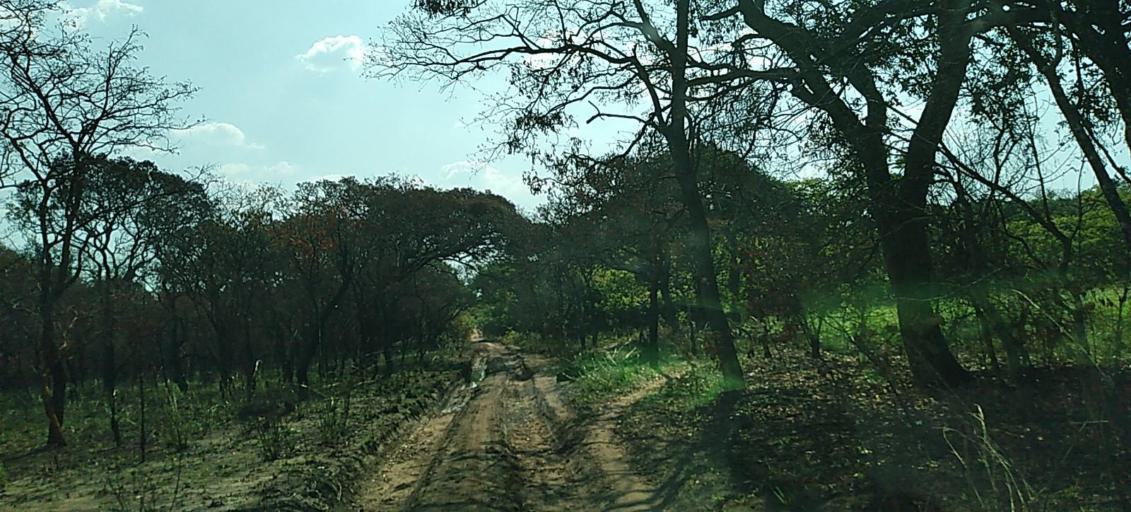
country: ZM
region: North-Western
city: Mwinilunga
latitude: -11.3010
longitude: 24.8463
